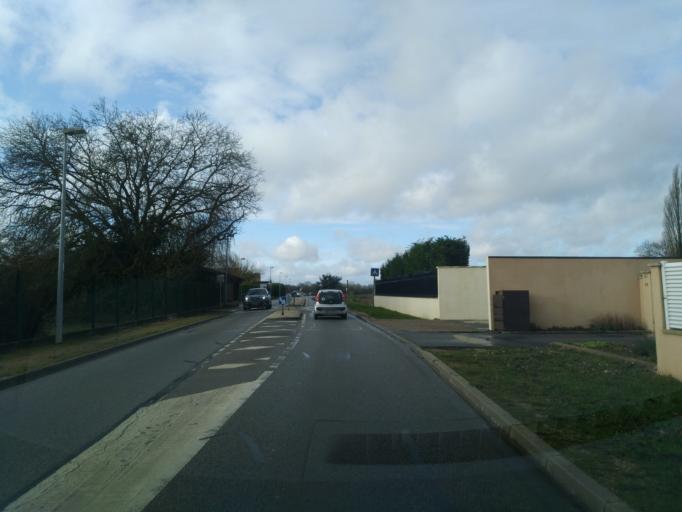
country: FR
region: Ile-de-France
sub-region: Departement des Yvelines
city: Les Alluets-le-Roi
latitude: 48.9138
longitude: 1.9136
